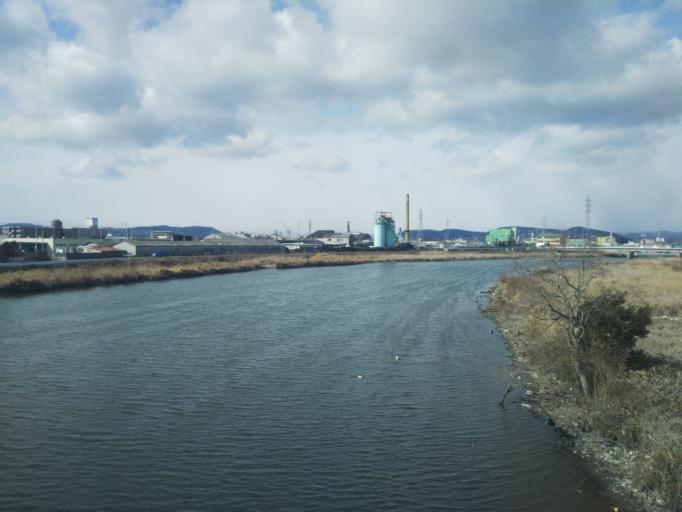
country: JP
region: Okayama
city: Okayama-shi
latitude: 34.6169
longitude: 133.8852
